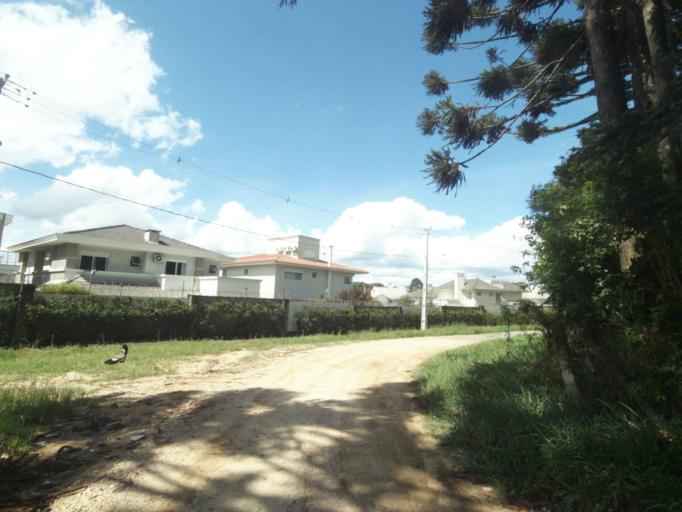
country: BR
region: Parana
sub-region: Curitiba
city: Curitiba
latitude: -25.4346
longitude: -49.3362
